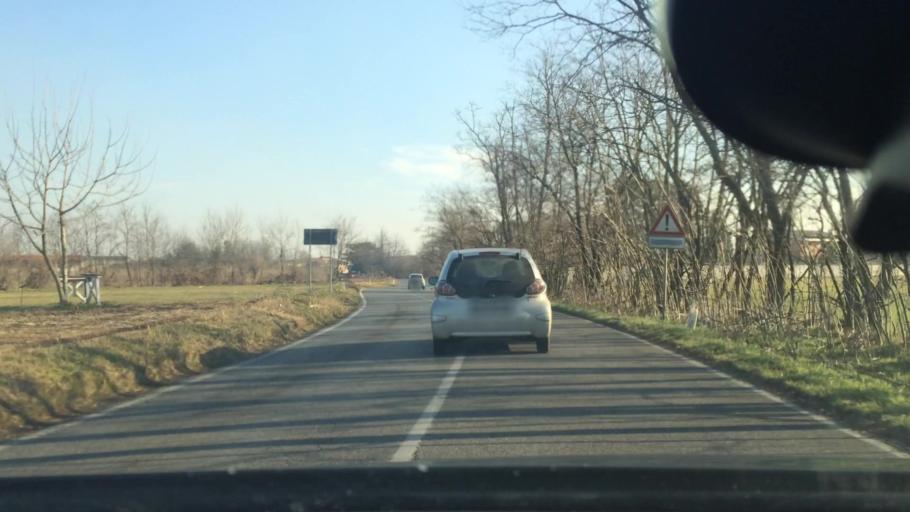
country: IT
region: Lombardy
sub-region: Citta metropolitana di Milano
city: Arluno
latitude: 45.5117
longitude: 8.9248
